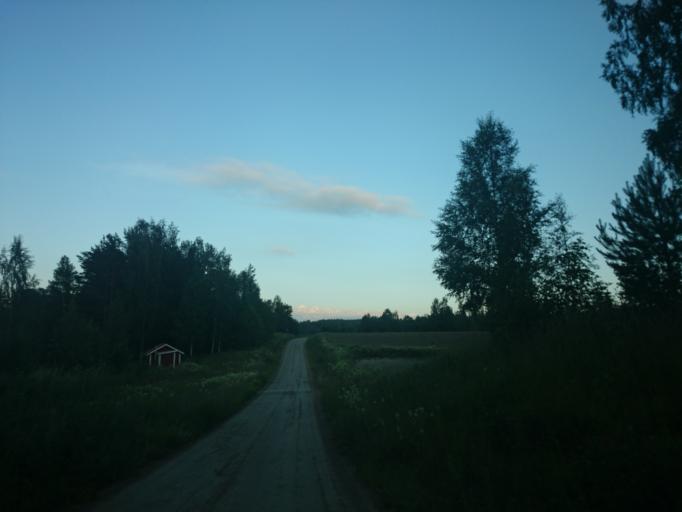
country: SE
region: Vaesternorrland
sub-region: Sundsvalls Kommun
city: Vi
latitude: 62.2070
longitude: 17.2619
